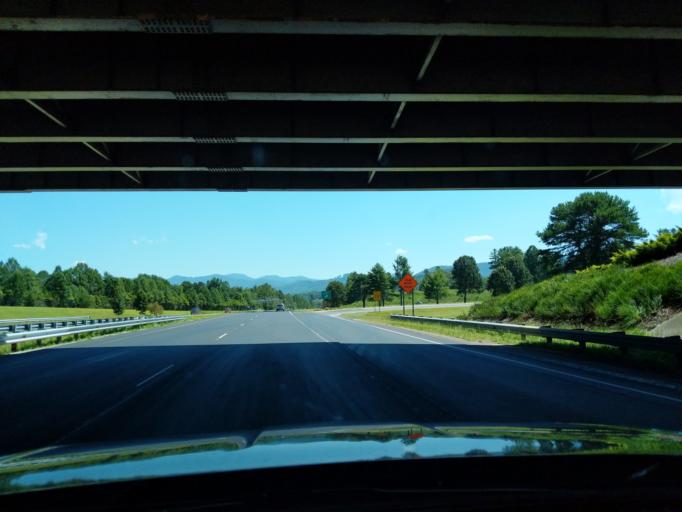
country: US
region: North Carolina
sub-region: Macon County
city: Franklin
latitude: 35.1664
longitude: -83.3910
